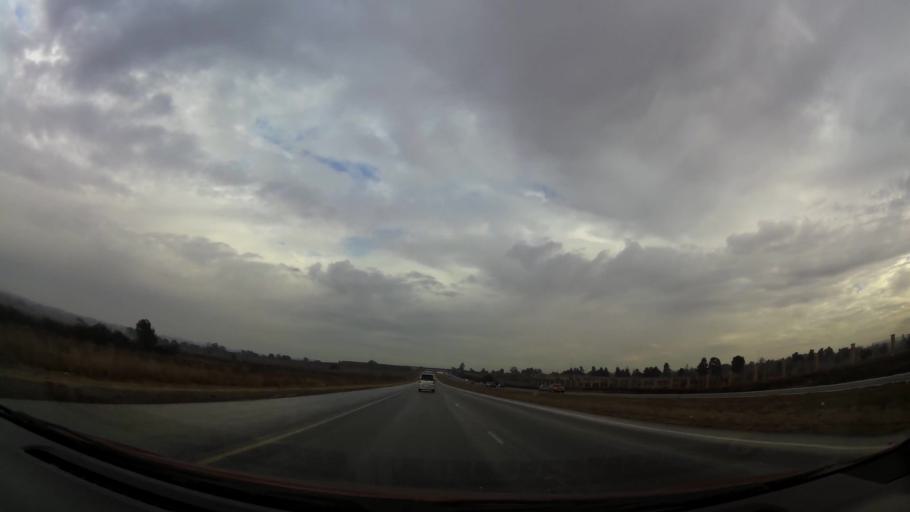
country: ZA
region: Gauteng
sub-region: City of Johannesburg Metropolitan Municipality
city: Soweto
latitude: -26.3015
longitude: 27.8574
